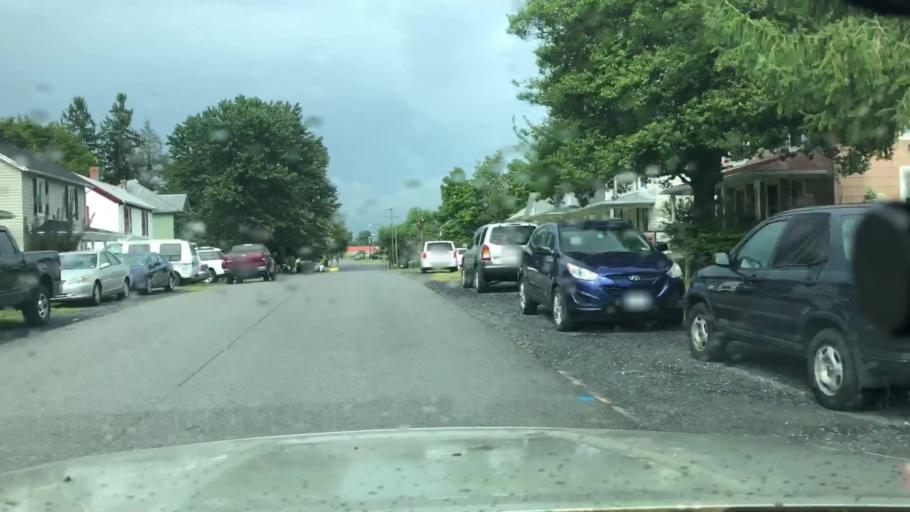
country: US
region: Virginia
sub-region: City of Waynesboro
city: Waynesboro
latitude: 38.0700
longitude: -78.9014
